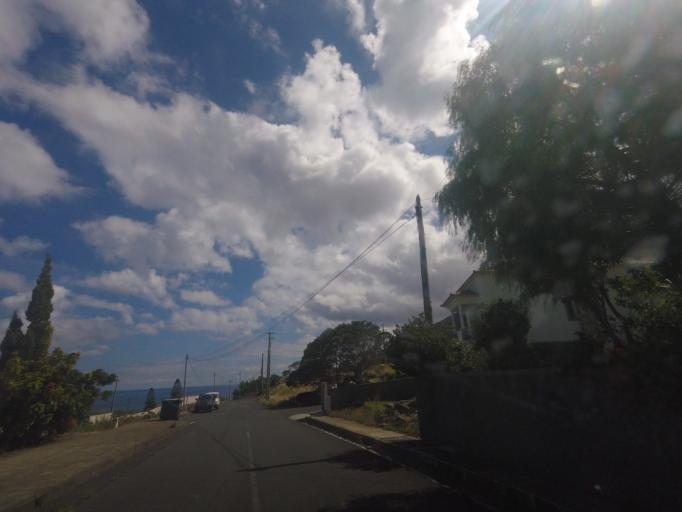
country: PT
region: Madeira
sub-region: Machico
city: Canical
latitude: 32.7382
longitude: -16.7456
